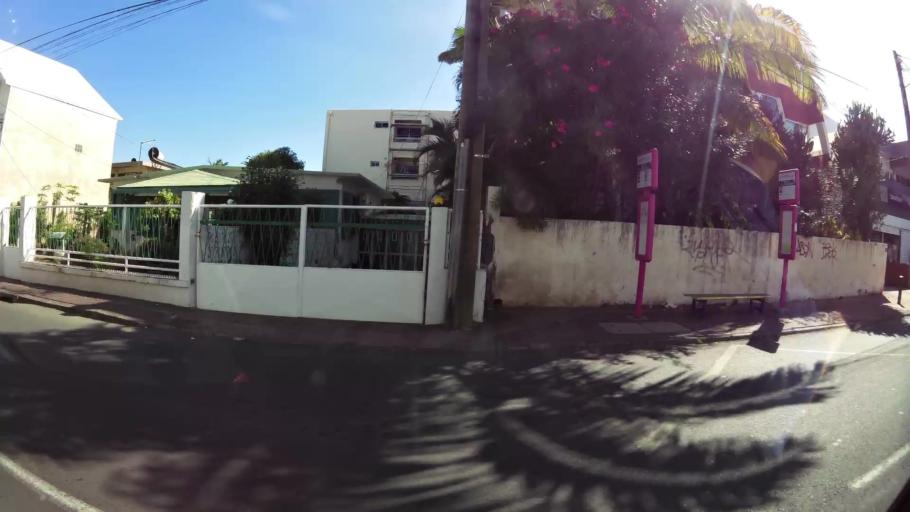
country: RE
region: Reunion
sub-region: Reunion
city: Saint-Pierre
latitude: -21.3401
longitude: 55.4691
